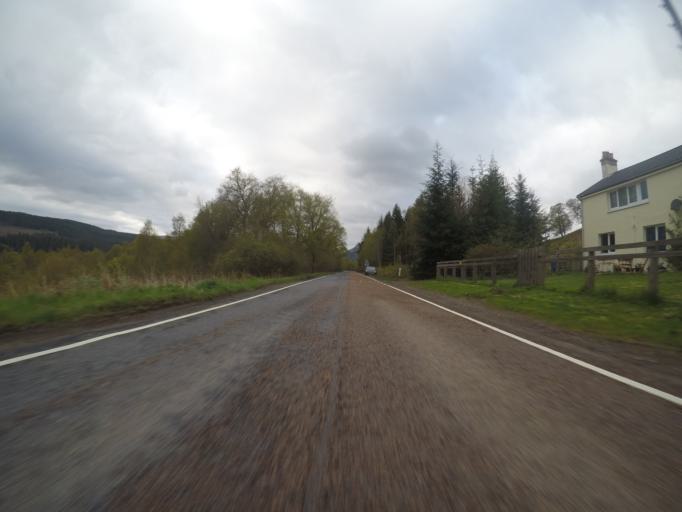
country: GB
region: Scotland
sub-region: Highland
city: Kingussie
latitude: 56.9699
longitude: -4.4372
